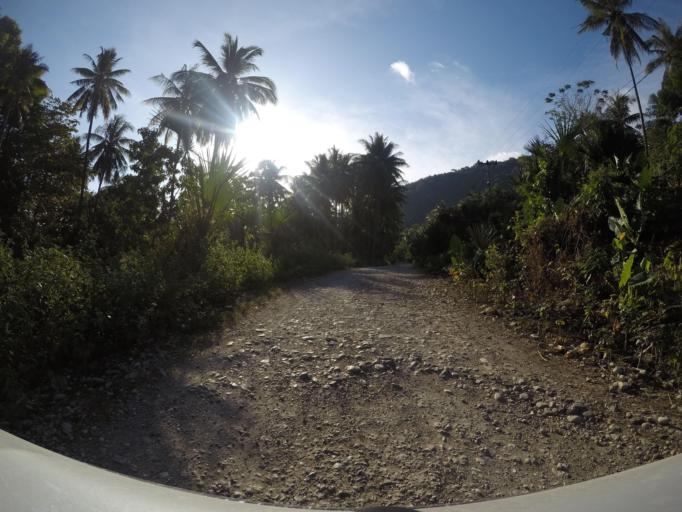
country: TL
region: Viqueque
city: Viqueque
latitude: -8.8030
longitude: 126.5689
